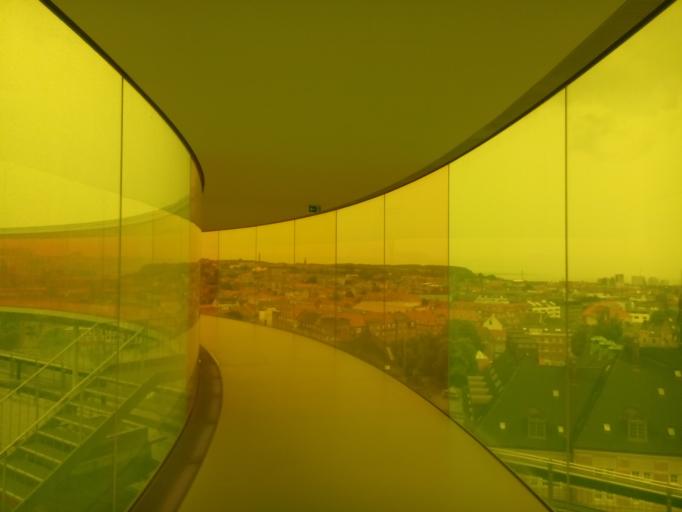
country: DK
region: Central Jutland
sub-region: Arhus Kommune
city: Arhus
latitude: 56.1539
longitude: 10.2001
